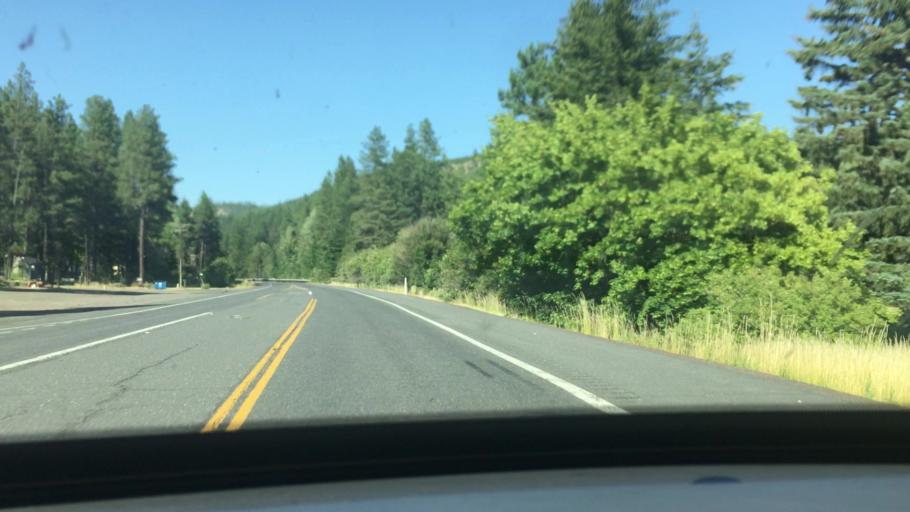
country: US
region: Washington
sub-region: Klickitat County
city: Goldendale
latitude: 45.9499
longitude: -120.6652
